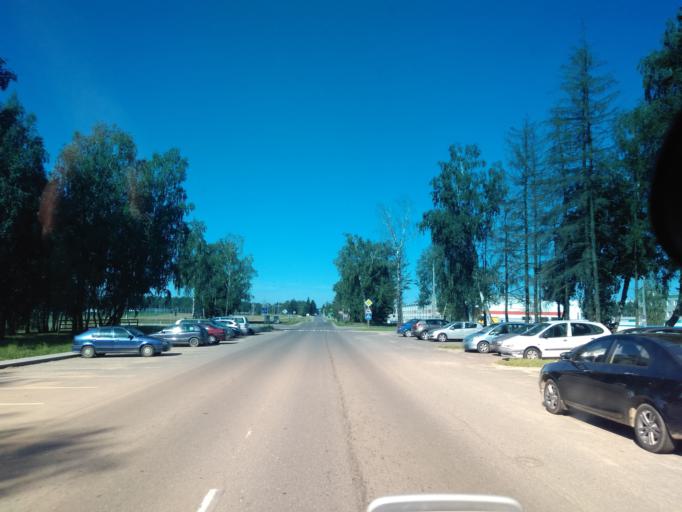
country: BY
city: Fanipol
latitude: 53.7406
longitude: 27.3581
